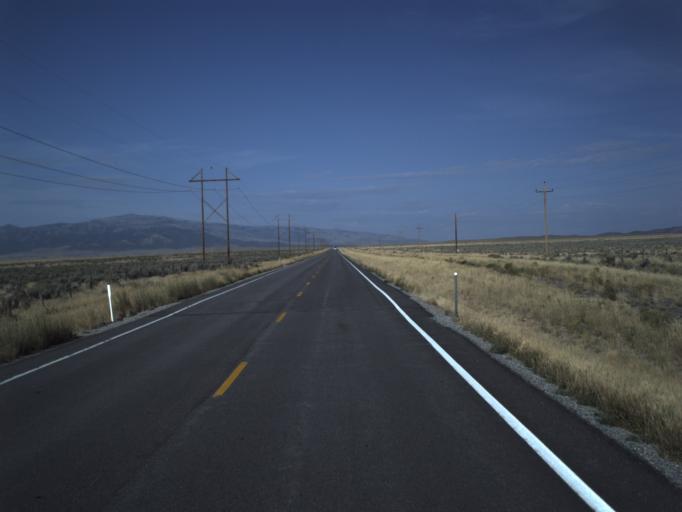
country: US
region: Idaho
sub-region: Oneida County
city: Malad City
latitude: 41.9658
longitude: -113.0026
